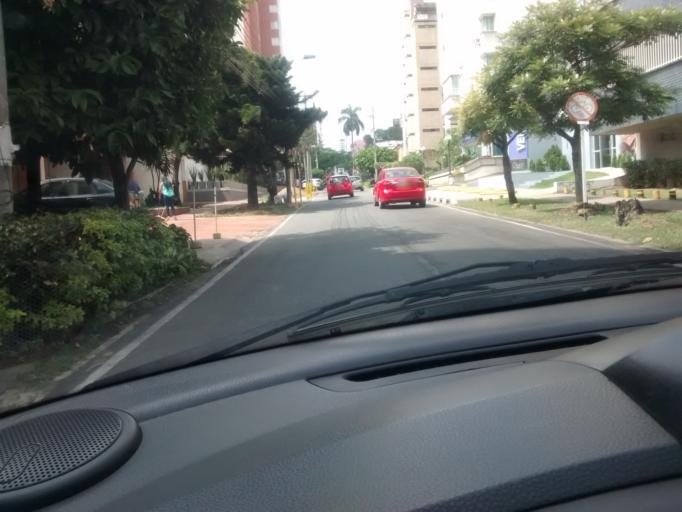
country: CO
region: Santander
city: Bucaramanga
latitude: 7.1196
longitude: -73.1092
